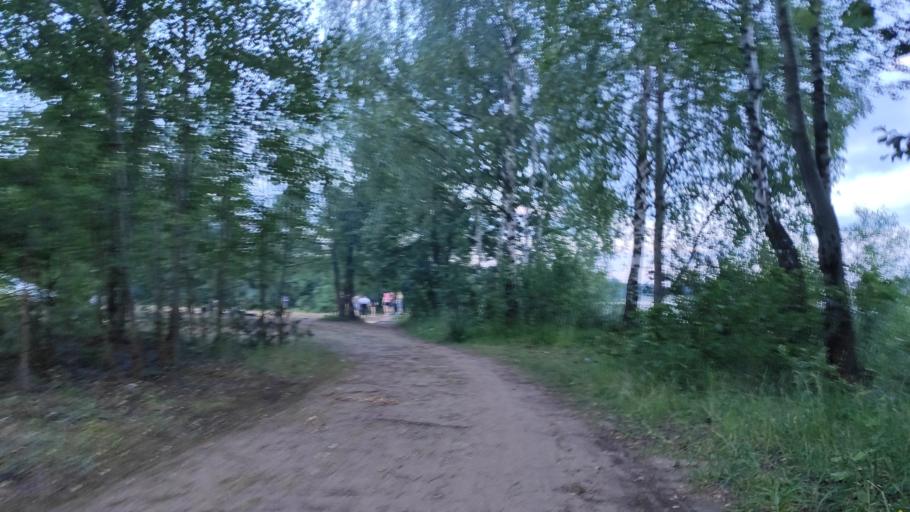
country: BY
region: Minsk
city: Zhdanovichy
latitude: 53.9500
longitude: 27.4786
